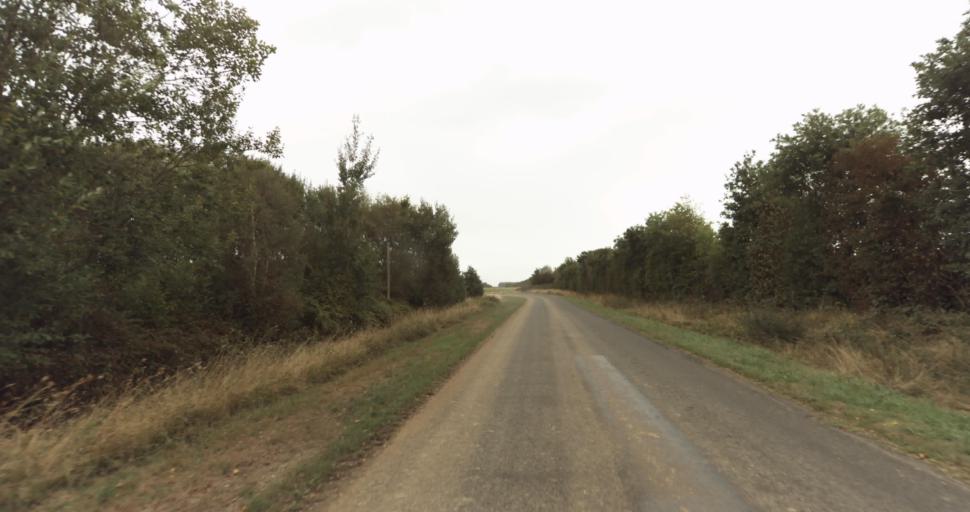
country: FR
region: Lower Normandy
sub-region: Departement de l'Orne
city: Gace
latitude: 48.8034
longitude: 0.3422
